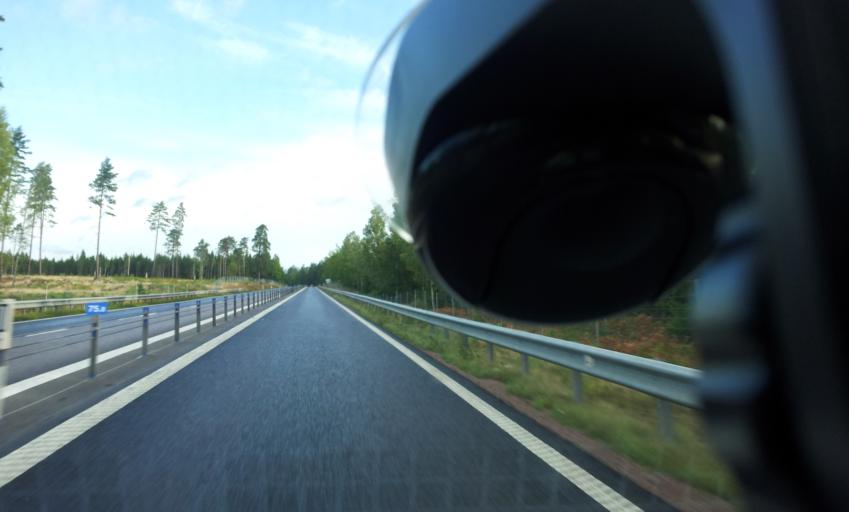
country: SE
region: Kalmar
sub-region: Monsteras Kommun
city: Timmernabben
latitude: 56.8788
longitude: 16.3827
